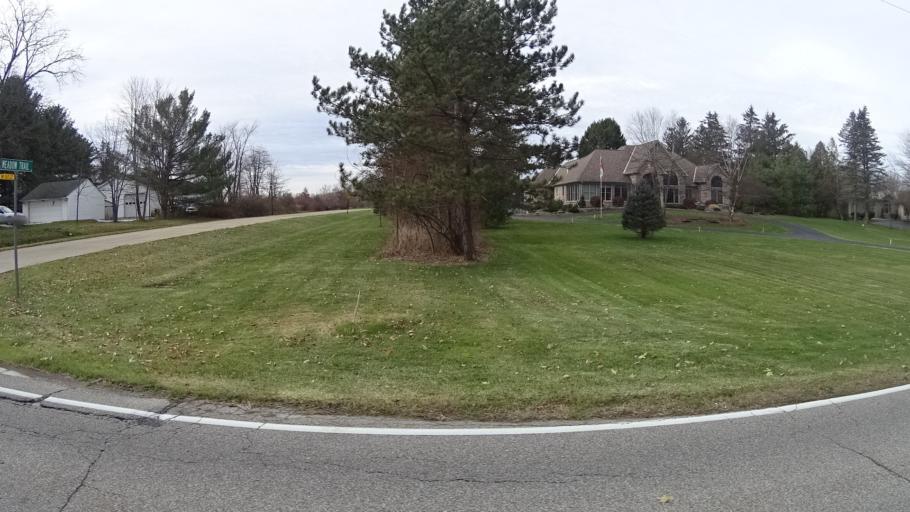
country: US
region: Ohio
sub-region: Cuyahoga County
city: Olmsted Falls
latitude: 41.2977
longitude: -81.9257
